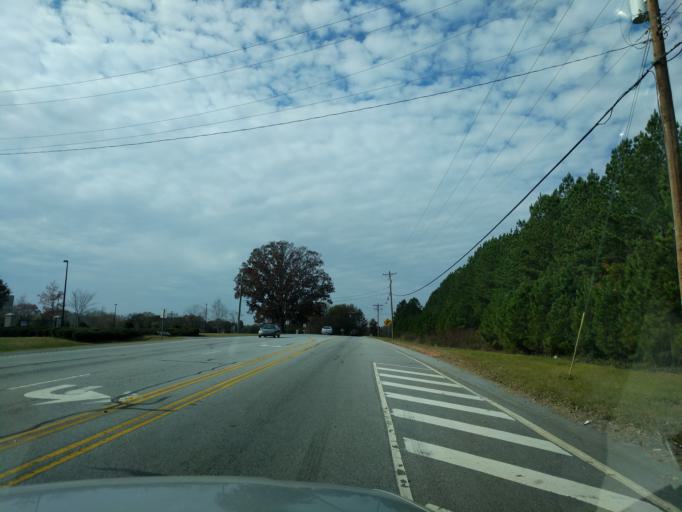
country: US
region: South Carolina
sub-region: Anderson County
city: Piedmont
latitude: 34.7101
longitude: -82.5034
